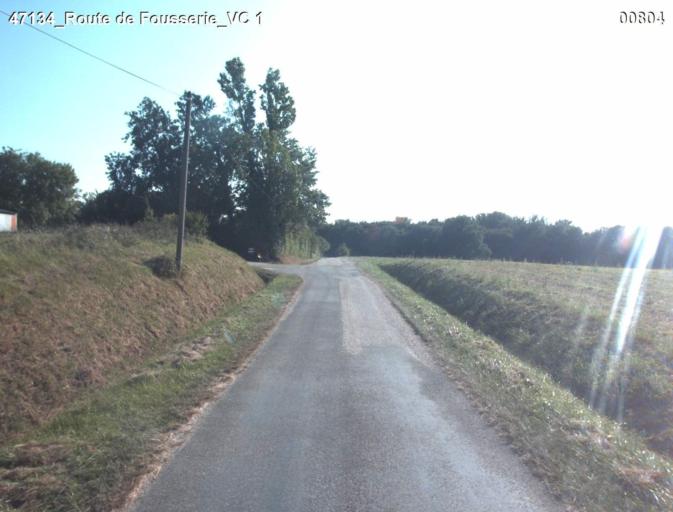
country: FR
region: Aquitaine
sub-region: Departement du Lot-et-Garonne
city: Mezin
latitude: 44.0262
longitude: 0.2785
